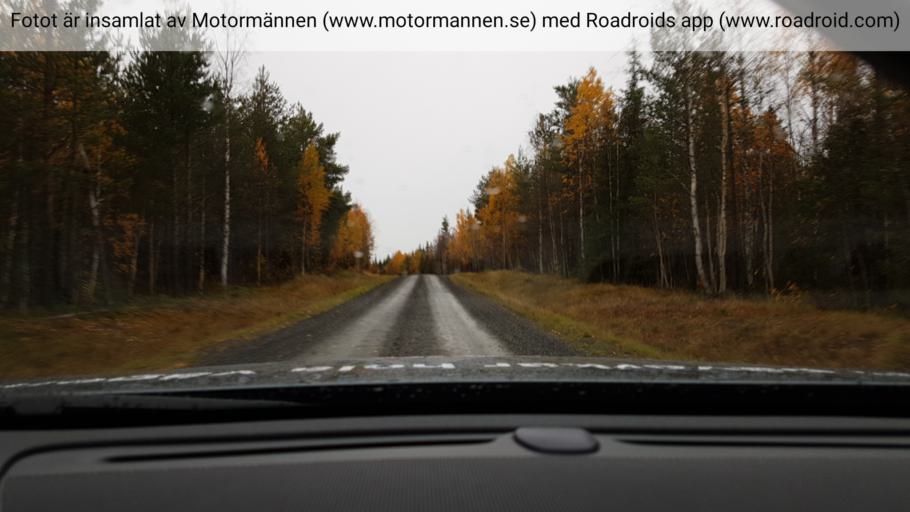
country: SE
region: Norrbotten
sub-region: Pajala Kommun
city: Pajala
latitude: 67.0594
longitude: 22.8315
